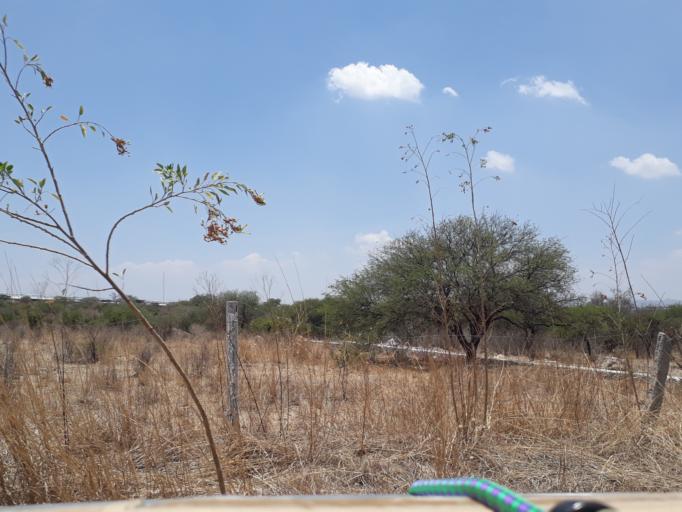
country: MX
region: Aguascalientes
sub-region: Aguascalientes
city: San Sebastian [Fraccionamiento]
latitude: 21.7791
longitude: -102.3305
